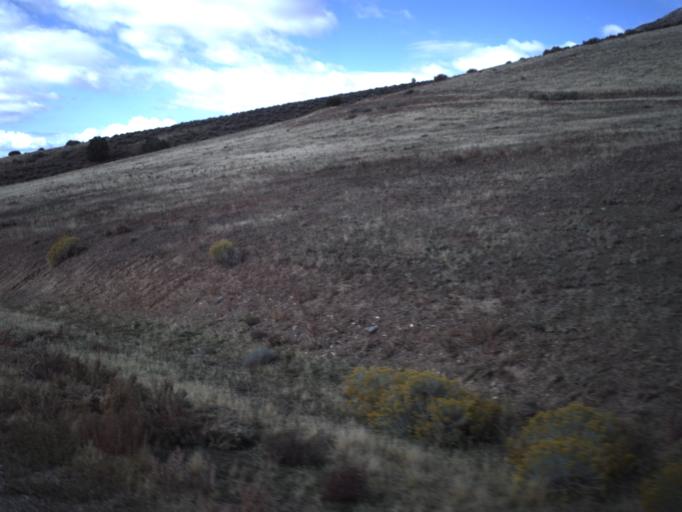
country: US
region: Utah
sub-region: Beaver County
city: Milford
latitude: 38.4469
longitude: -113.2623
